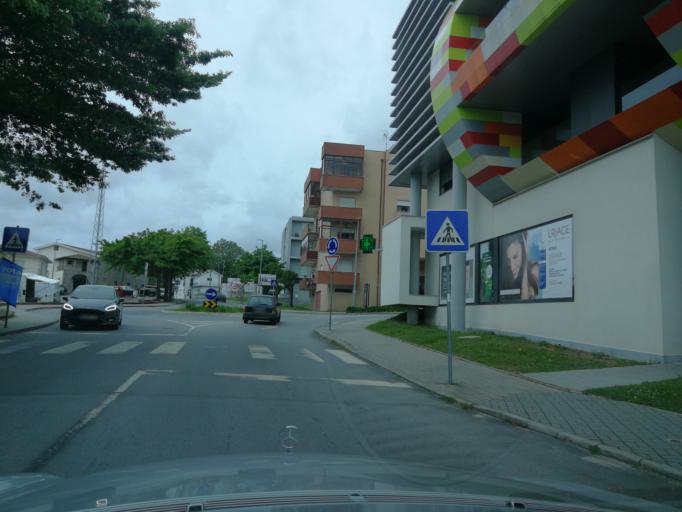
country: PT
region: Braga
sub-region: Amares
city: Amares
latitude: 41.6258
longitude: -8.3623
